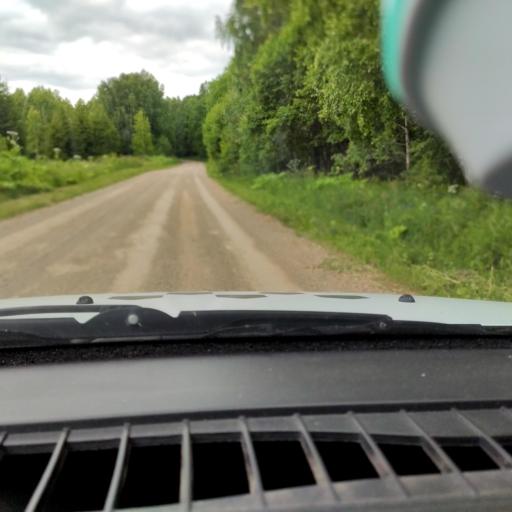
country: RU
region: Perm
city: Suksun
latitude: 57.2090
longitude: 57.6417
